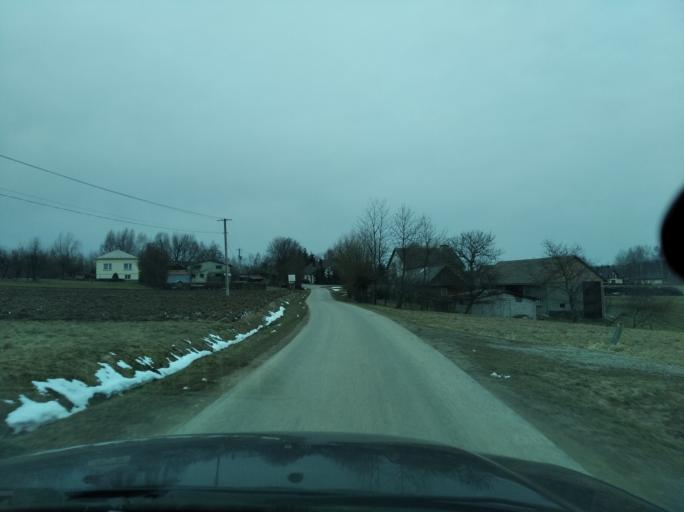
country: PL
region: Subcarpathian Voivodeship
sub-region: Powiat rzeszowski
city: Chmielnik
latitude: 49.9908
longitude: 22.1456
